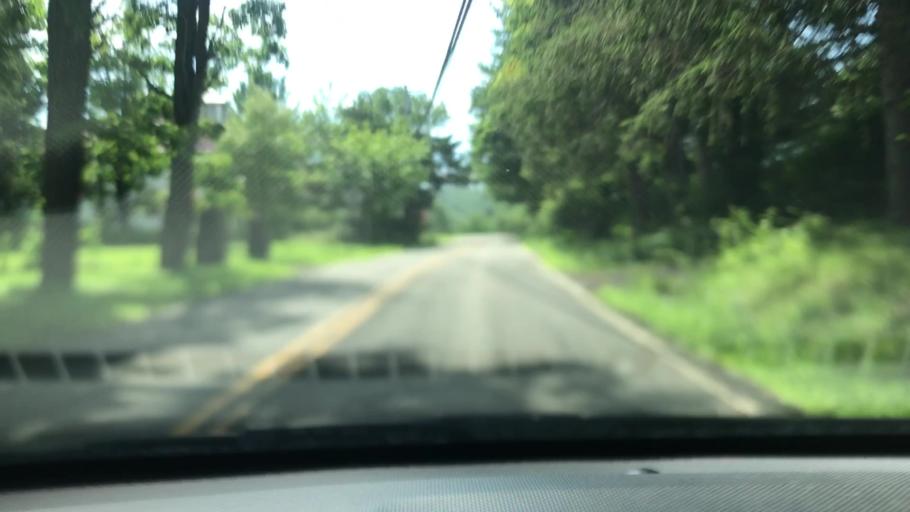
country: US
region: New York
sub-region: Ulster County
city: Shokan
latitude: 41.9208
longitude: -74.2141
